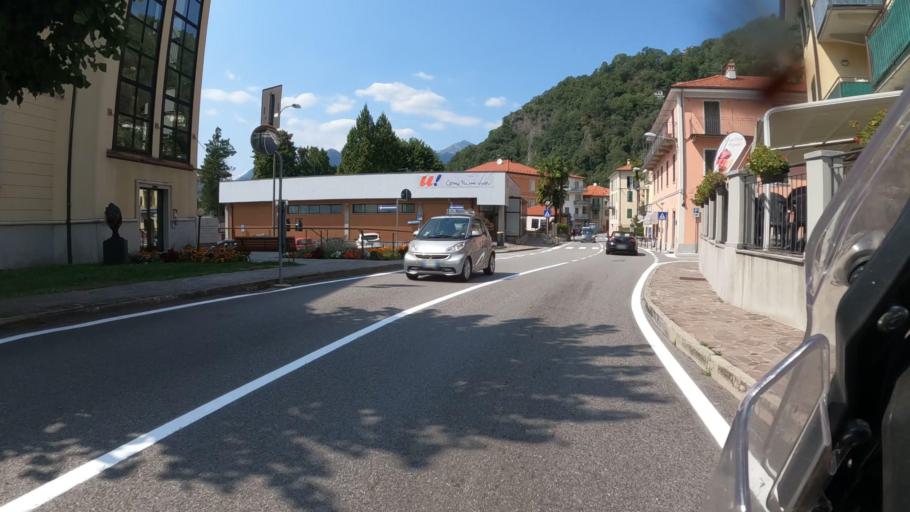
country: IT
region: Lombardy
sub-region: Provincia di Varese
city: Maccagno
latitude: 46.0426
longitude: 8.7387
